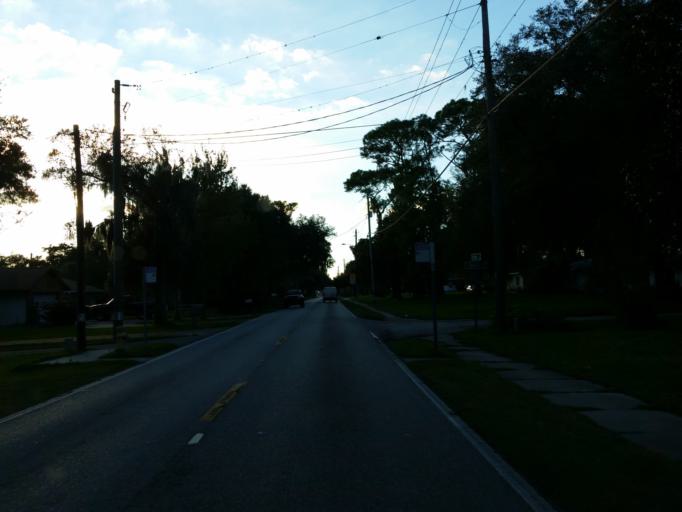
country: US
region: Florida
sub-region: Hillsborough County
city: Riverview
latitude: 27.8718
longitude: -82.3212
